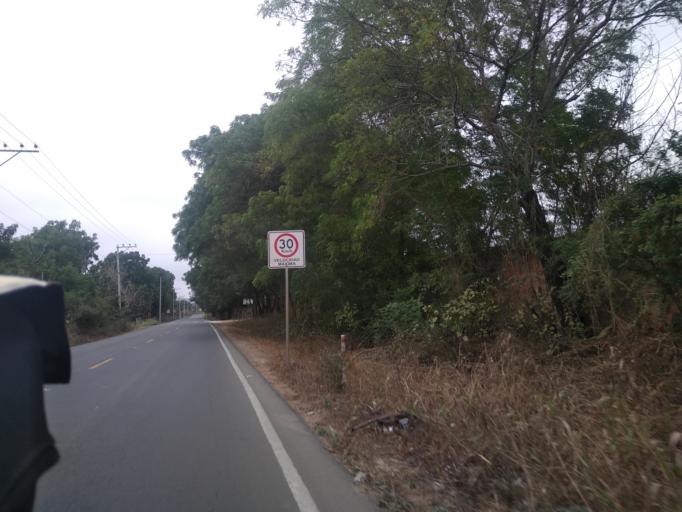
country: EC
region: Manabi
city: Montecristi
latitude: -1.0714
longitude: -80.6628
